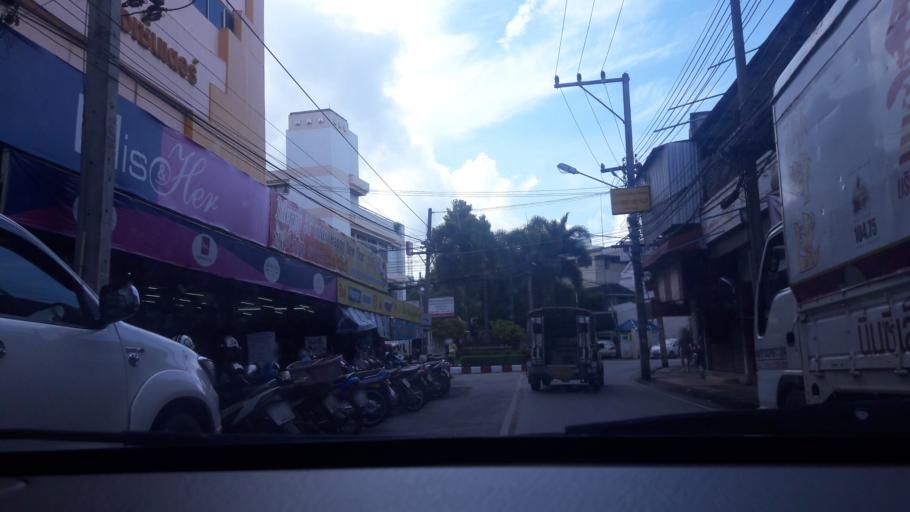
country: TH
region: Chiang Mai
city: Chiang Mai
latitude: 18.7890
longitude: 99.0014
